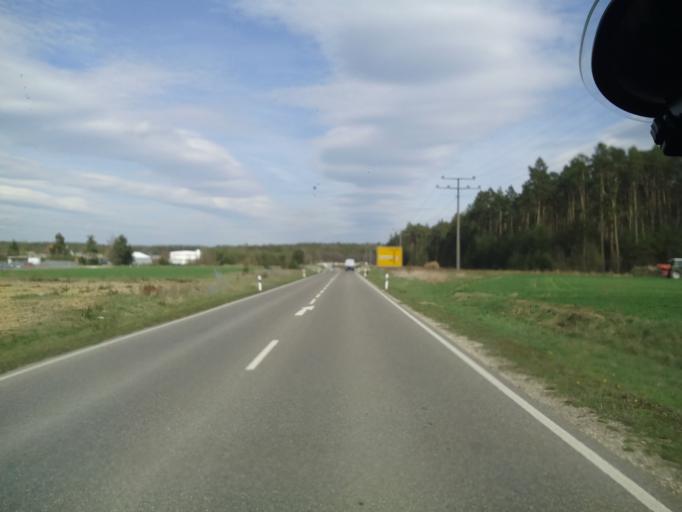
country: DE
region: Bavaria
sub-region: Regierungsbezirk Mittelfranken
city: Georgensgmund
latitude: 49.1685
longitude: 11.0045
